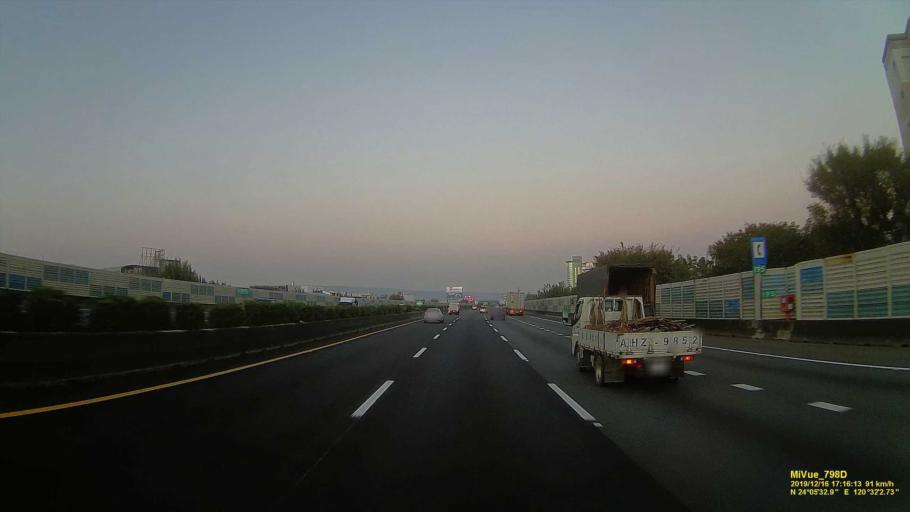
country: TW
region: Taiwan
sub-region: Changhua
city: Chang-hua
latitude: 24.0940
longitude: 120.5345
